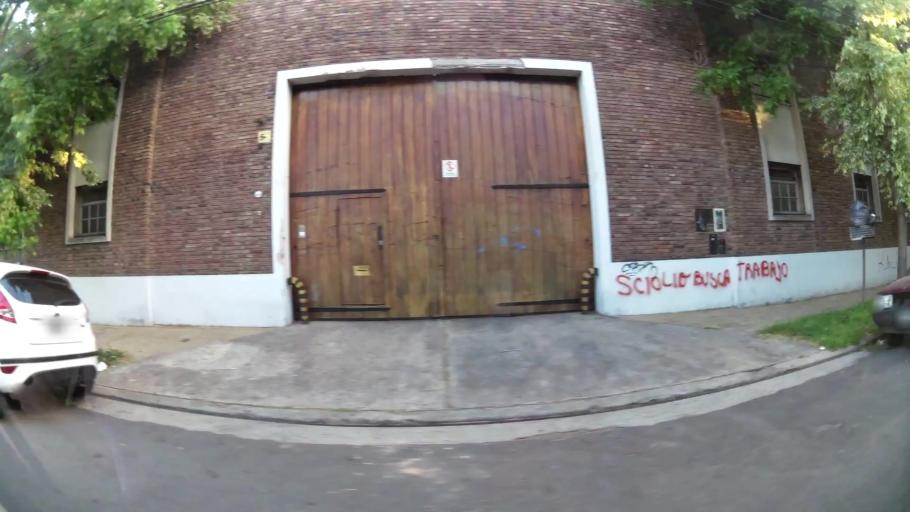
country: AR
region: Buenos Aires
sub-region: Partido de General San Martin
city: General San Martin
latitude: -34.5405
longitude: -58.5035
